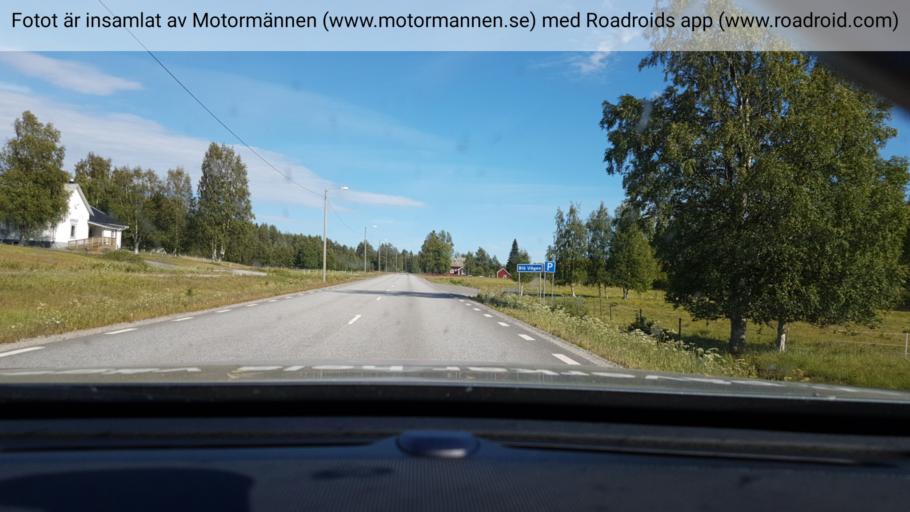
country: SE
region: Vaesterbotten
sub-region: Lycksele Kommun
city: Lycksele
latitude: 64.6976
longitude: 18.3770
